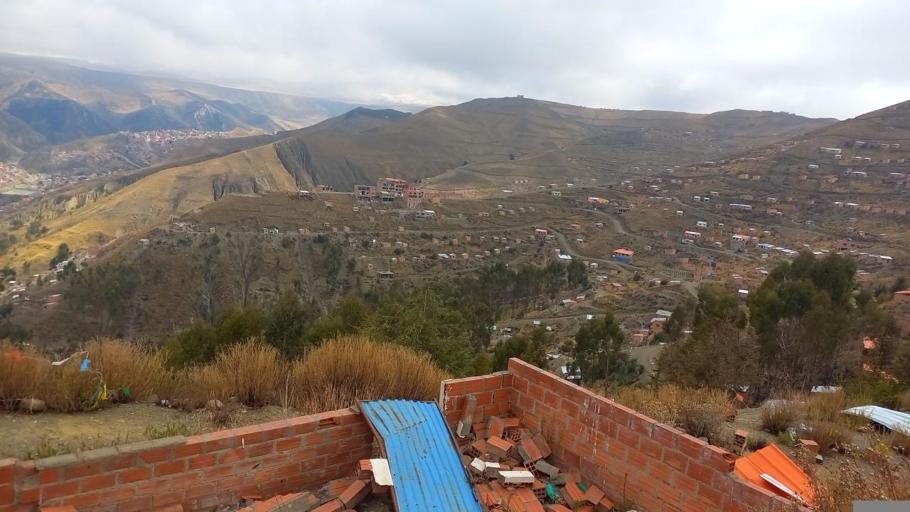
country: BO
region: La Paz
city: La Paz
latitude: -16.4654
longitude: -68.1427
